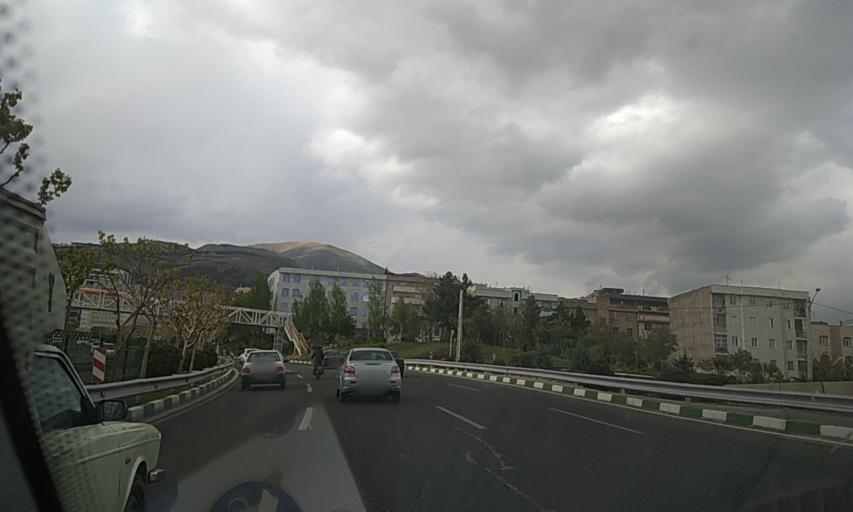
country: IR
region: Tehran
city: Tajrish
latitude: 35.7736
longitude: 51.3205
